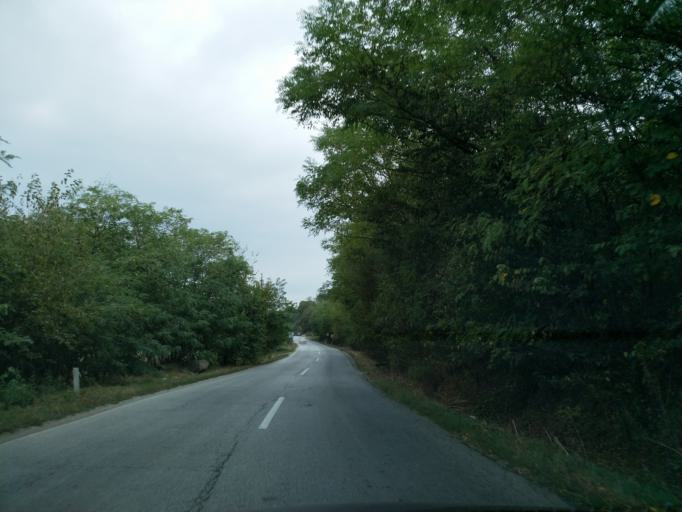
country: RS
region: Central Serbia
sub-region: Pomoravski Okrug
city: Jagodina
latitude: 44.0363
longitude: 21.1896
